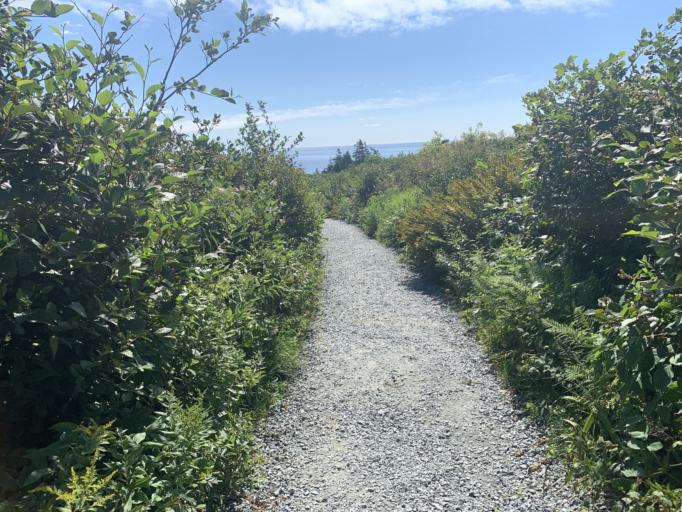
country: CA
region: Nova Scotia
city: Shelburne
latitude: 43.8283
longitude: -64.8394
